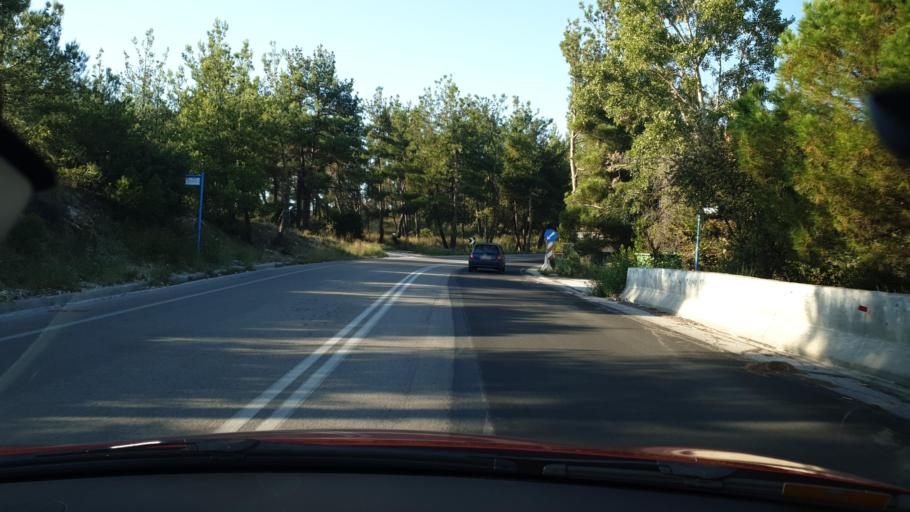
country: GR
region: Central Macedonia
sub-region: Nomos Thessalonikis
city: Panorama
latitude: 40.6110
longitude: 23.0560
